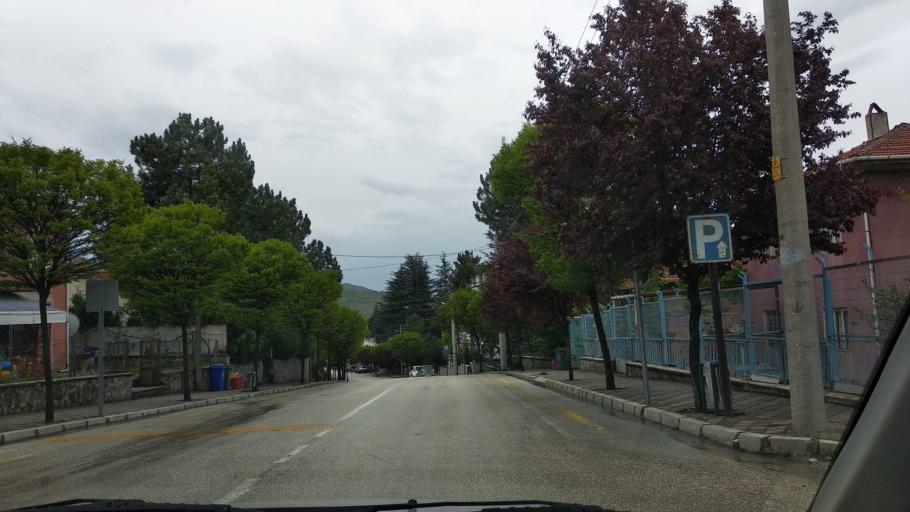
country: TR
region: Bolu
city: Seben
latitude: 40.4118
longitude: 31.5736
